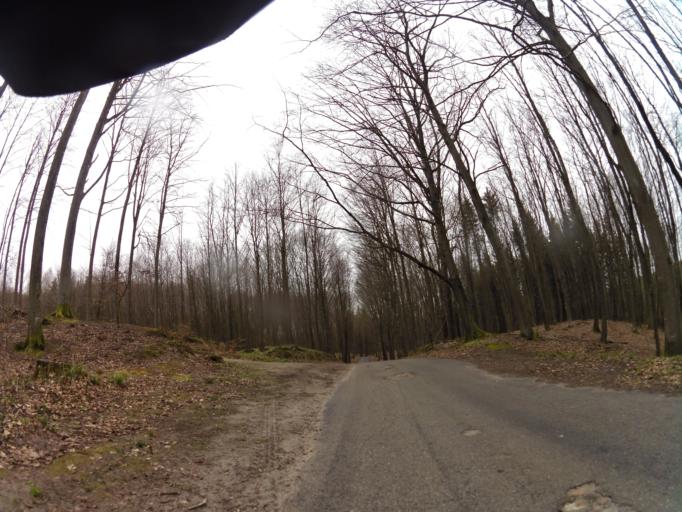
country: PL
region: West Pomeranian Voivodeship
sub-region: Powiat koszalinski
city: Bobolice
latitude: 53.9560
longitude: 16.6627
